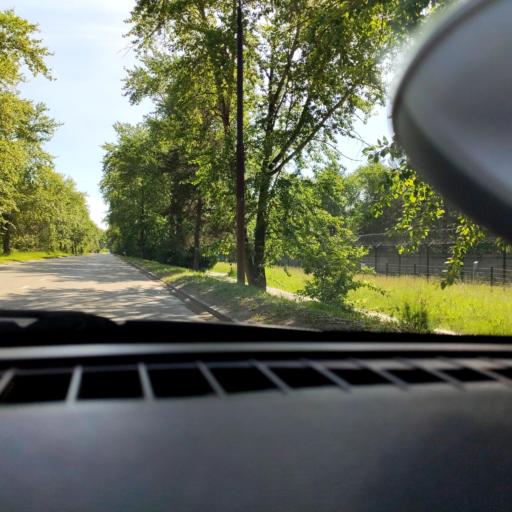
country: RU
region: Perm
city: Overyata
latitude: 57.9946
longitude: 55.8924
